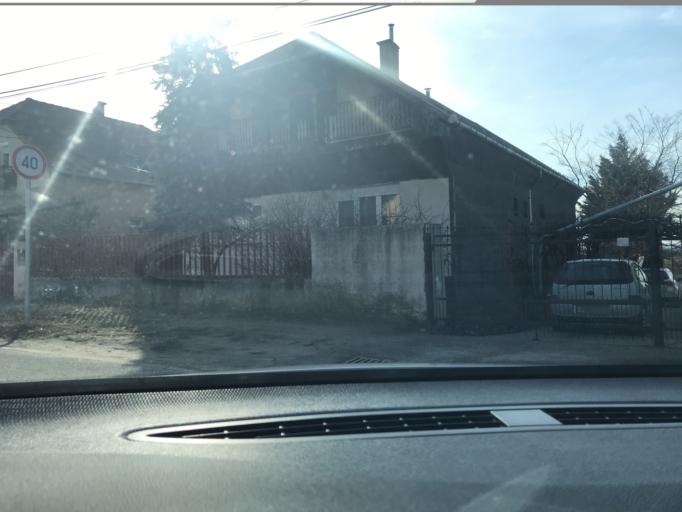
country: HU
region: Pest
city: Fot
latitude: 47.6262
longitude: 19.1745
